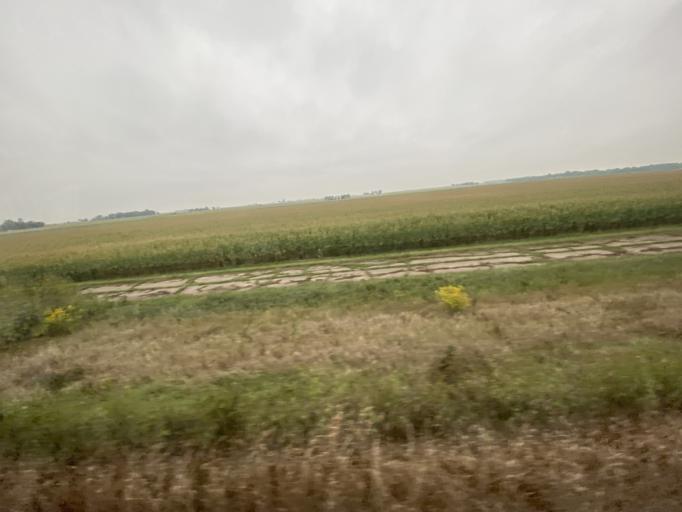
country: US
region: Illinois
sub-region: DeKalb County
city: Somonauk
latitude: 41.6237
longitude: -88.7418
